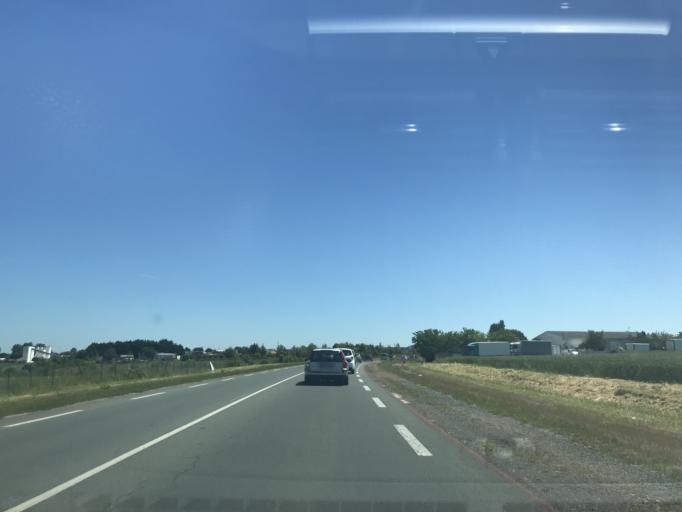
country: FR
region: Poitou-Charentes
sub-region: Departement de la Charente-Maritime
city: Saint-Georges-de-Didonne
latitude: 45.6099
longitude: -0.9777
